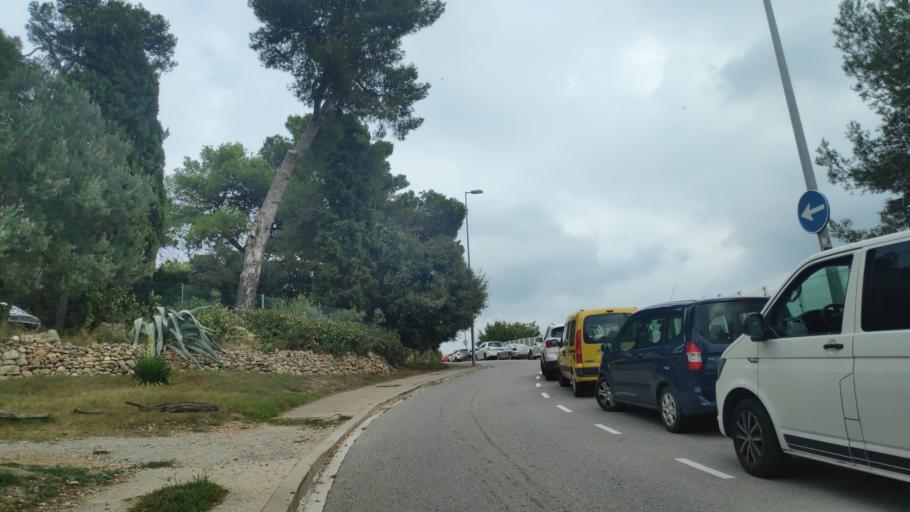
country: ES
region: Catalonia
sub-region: Provincia de Barcelona
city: Rubi
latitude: 41.4807
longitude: 2.0584
